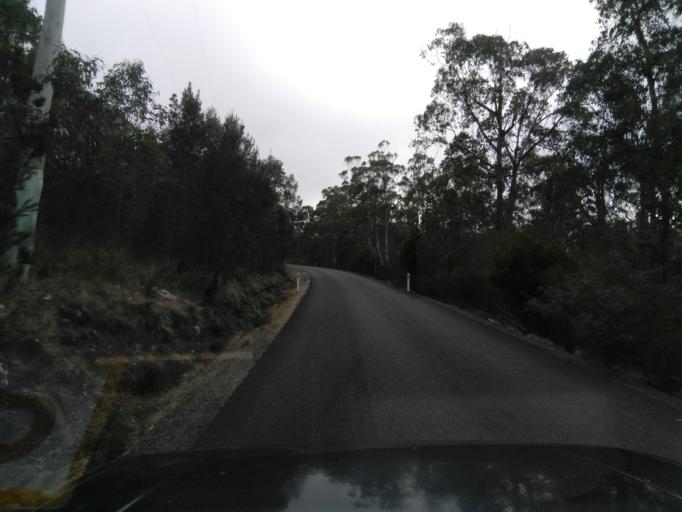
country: AU
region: Tasmania
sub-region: Kingborough
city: Taroona
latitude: -42.9506
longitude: 147.3219
